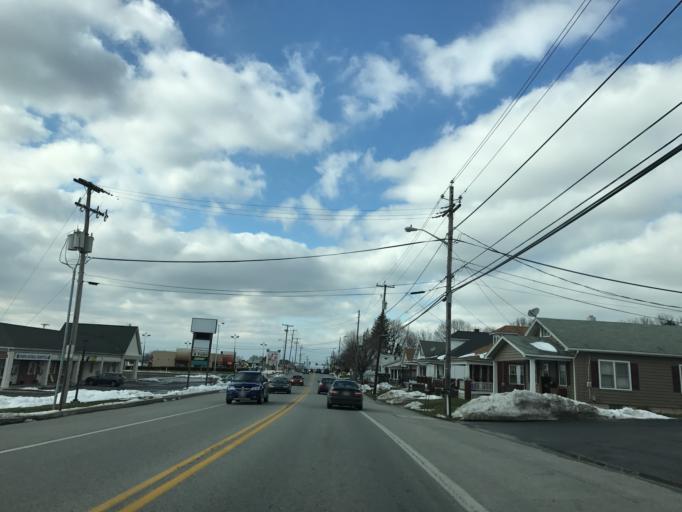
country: US
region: Pennsylvania
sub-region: York County
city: Parkville
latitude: 39.7785
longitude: -76.9614
